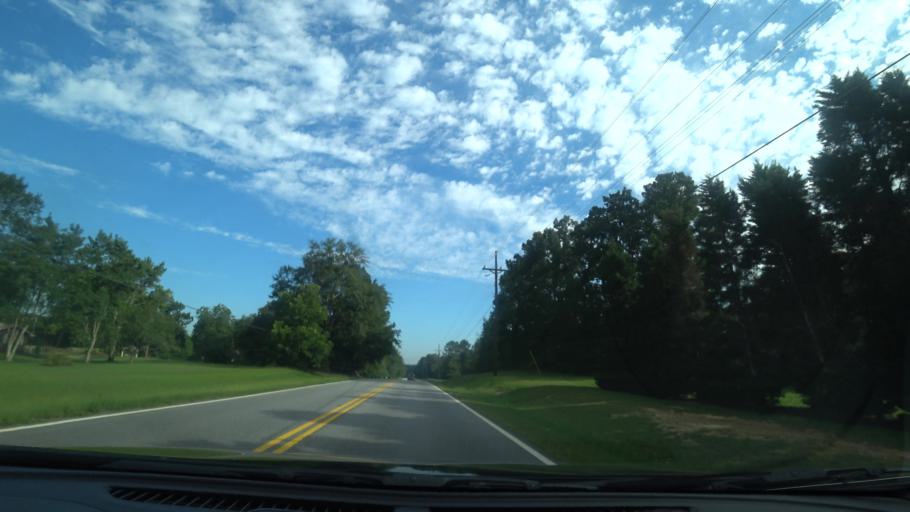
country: US
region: Georgia
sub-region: Rockdale County
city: Lakeview Estates
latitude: 33.7585
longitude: -83.9831
